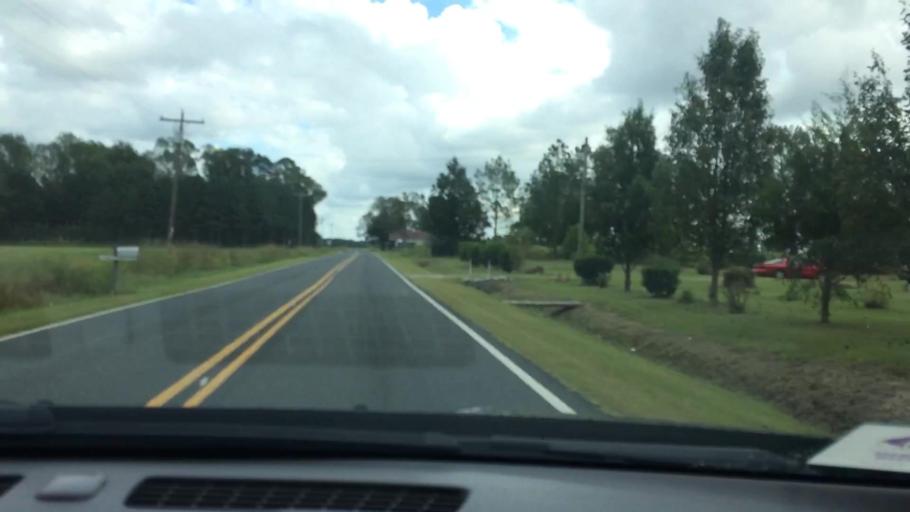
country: US
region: North Carolina
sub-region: Greene County
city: Maury
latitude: 35.5194
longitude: -77.5325
